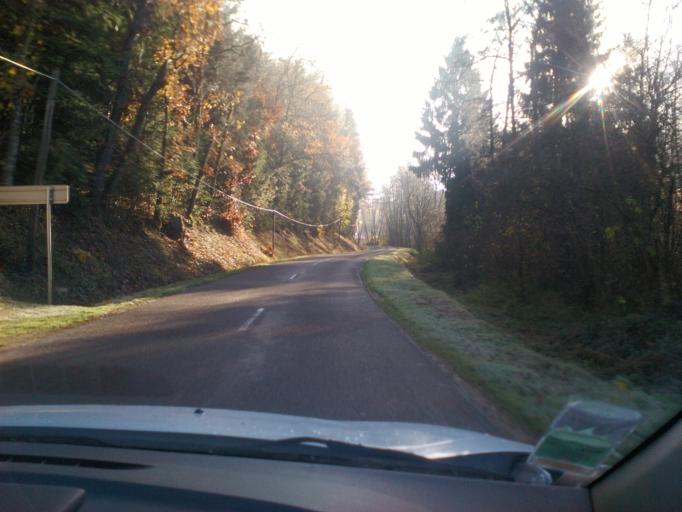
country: FR
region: Lorraine
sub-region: Departement des Vosges
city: Uzemain
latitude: 48.0626
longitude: 6.3329
